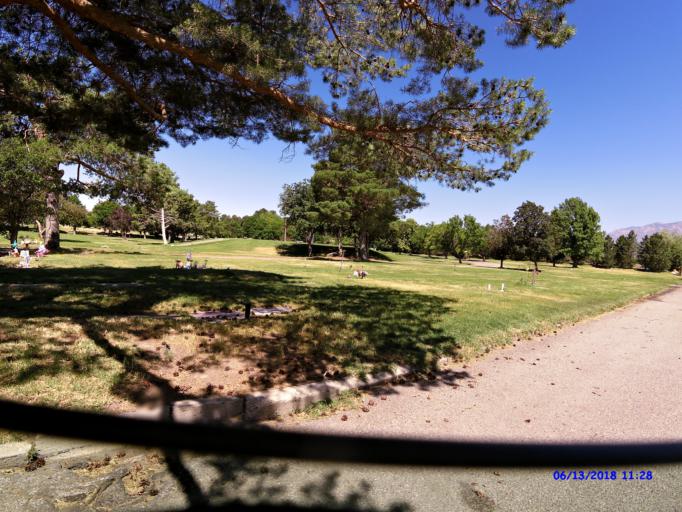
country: US
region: Utah
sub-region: Weber County
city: Ogden
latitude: 41.2332
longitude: -111.9602
